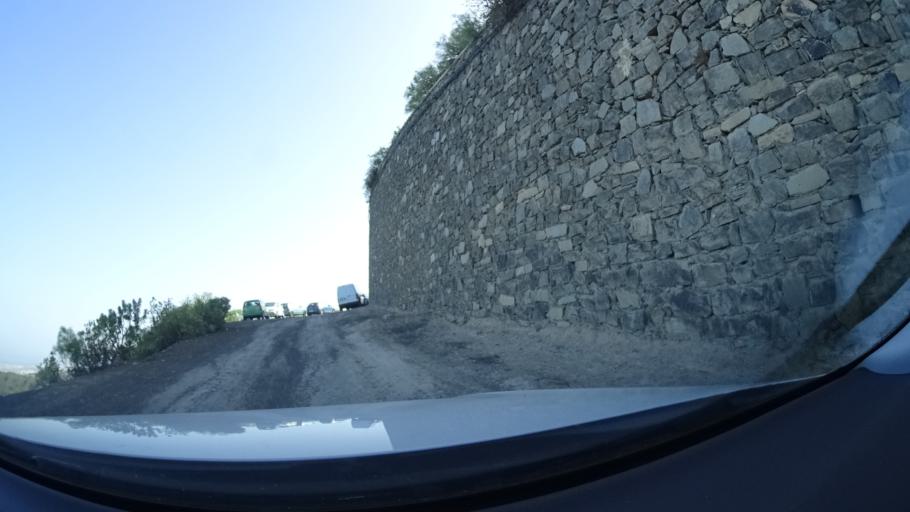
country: ES
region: Canary Islands
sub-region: Provincia de Las Palmas
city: Santa Brigida
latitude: 28.0321
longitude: -15.4595
